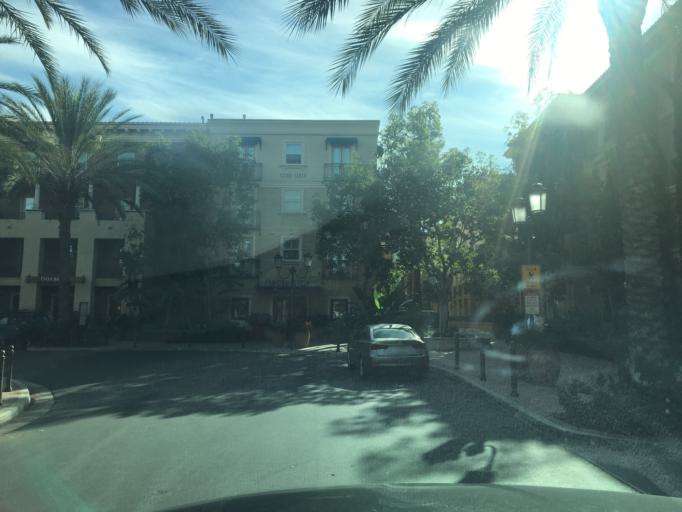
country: US
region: California
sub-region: Orange County
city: Laguna Woods
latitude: 33.6528
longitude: -117.7544
